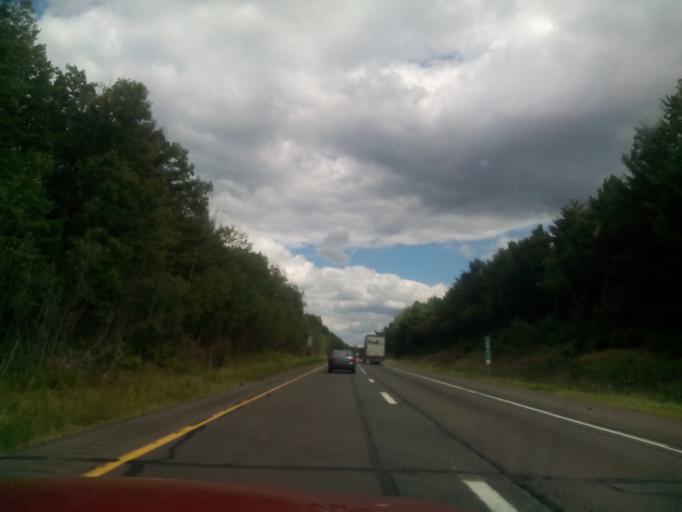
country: US
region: Pennsylvania
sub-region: Monroe County
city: Pocono Pines
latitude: 41.0781
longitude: -75.5231
